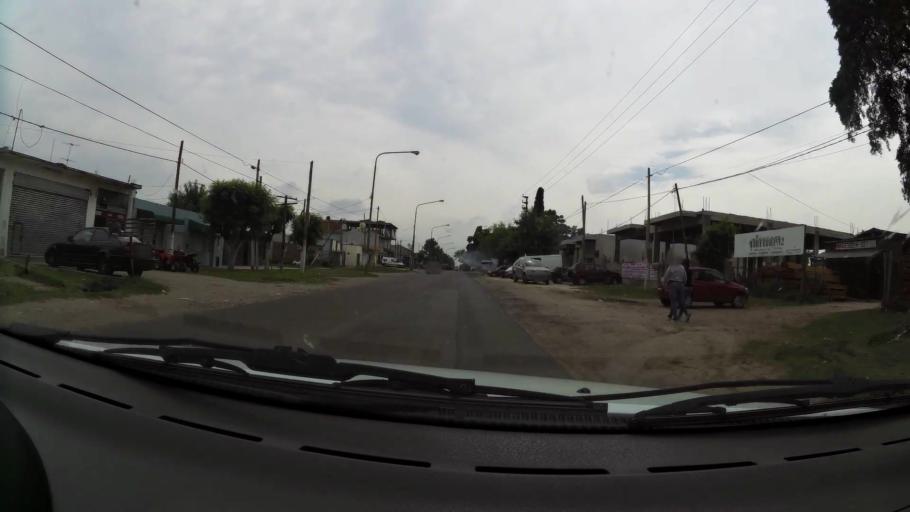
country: AR
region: Buenos Aires
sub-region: Partido de La Plata
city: La Plata
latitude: -34.9336
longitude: -58.0051
